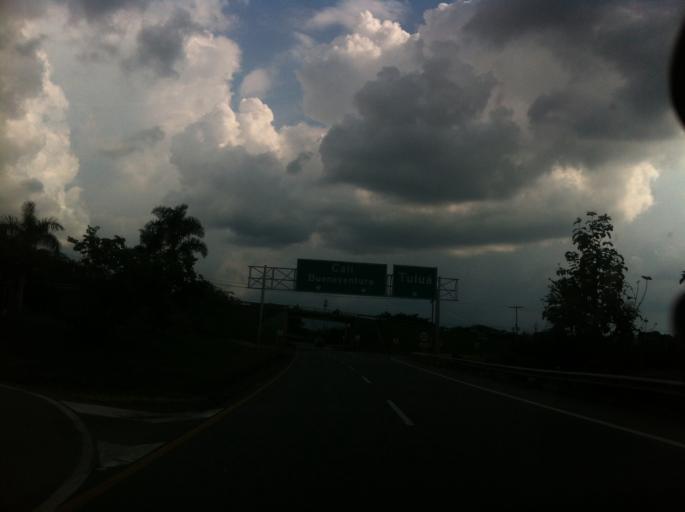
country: CO
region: Valle del Cauca
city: Tulua
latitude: 4.0984
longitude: -76.1763
